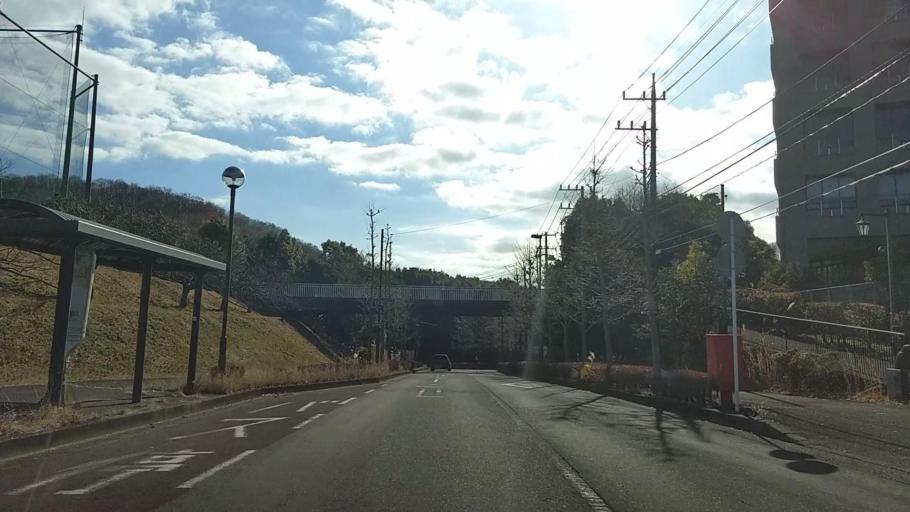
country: JP
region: Kanagawa
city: Atsugi
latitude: 35.4438
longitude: 139.3168
